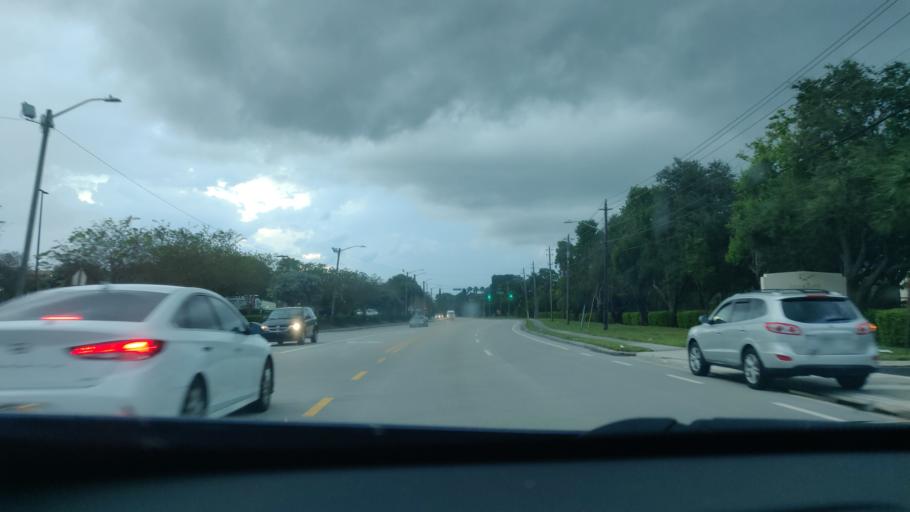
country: US
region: Florida
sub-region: Palm Beach County
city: Schall Circle
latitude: 26.7213
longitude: -80.1122
